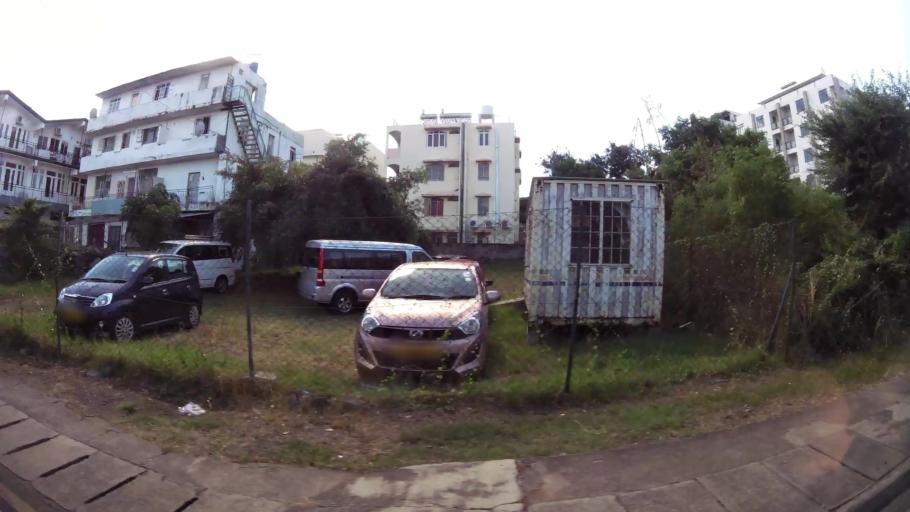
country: MU
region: Black River
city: Flic en Flac
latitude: -20.2764
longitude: 57.3732
